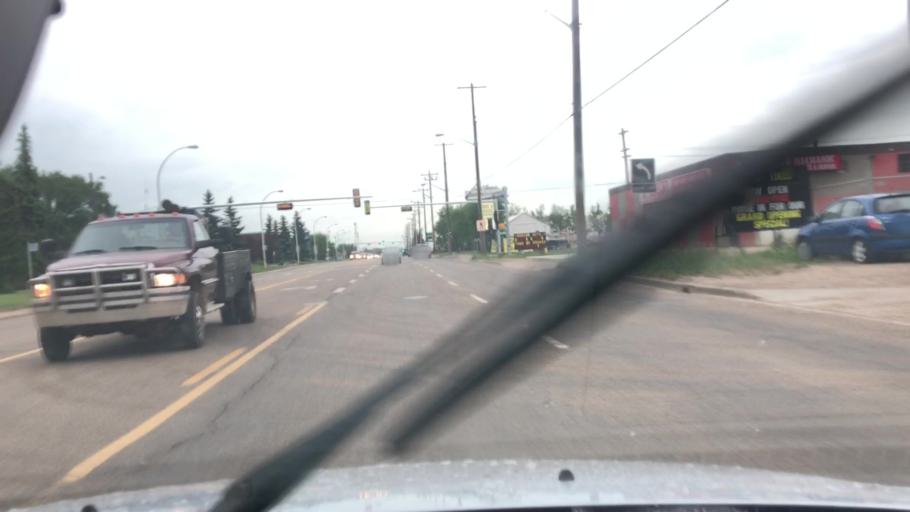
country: CA
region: Alberta
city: St. Albert
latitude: 53.5760
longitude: -113.5779
